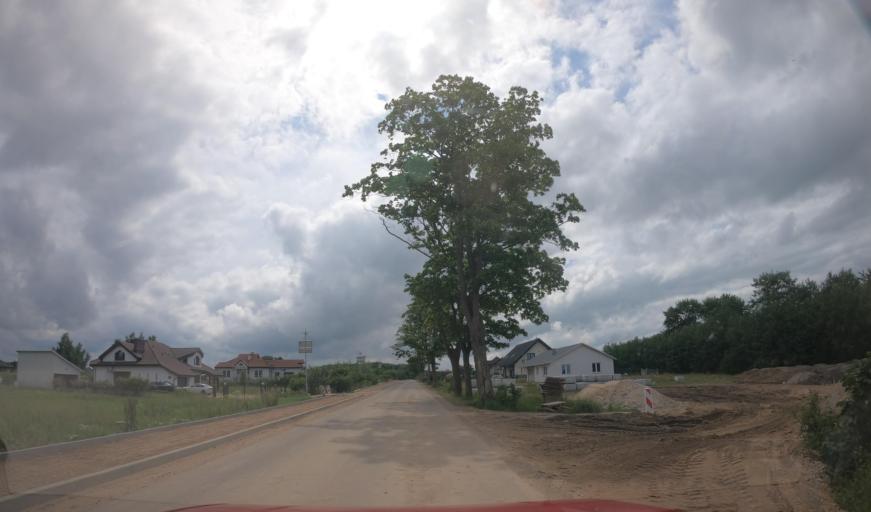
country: PL
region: West Pomeranian Voivodeship
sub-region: Powiat koszalinski
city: Mielno
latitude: 54.2243
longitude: 16.1035
